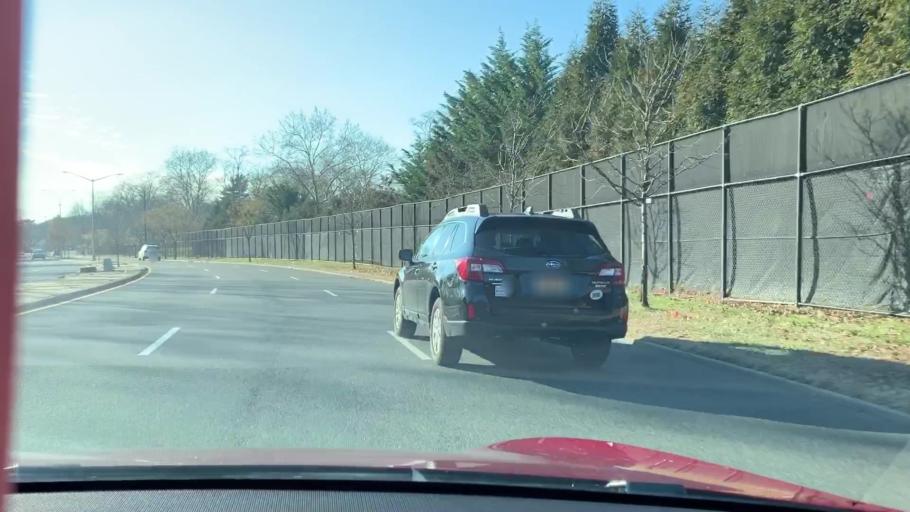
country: US
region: New York
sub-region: Nassau County
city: Bellerose Terrace
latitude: 40.7405
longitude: -73.7313
